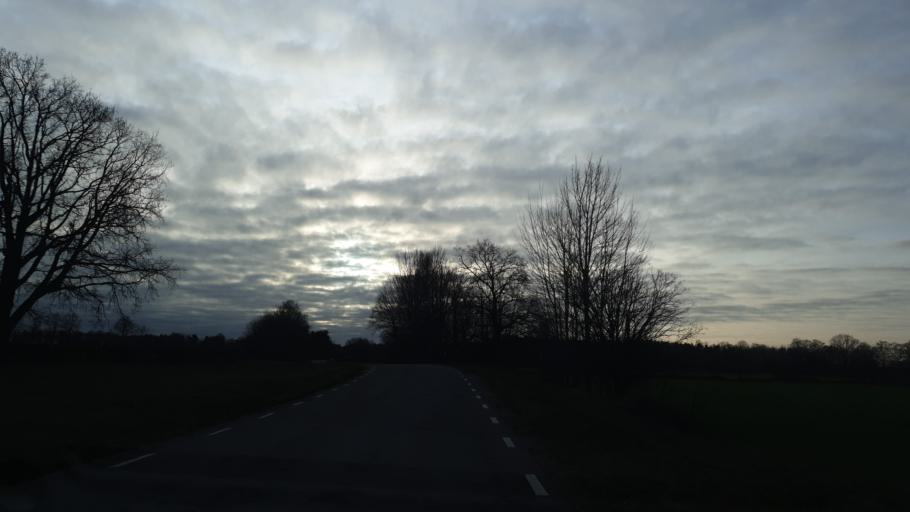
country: SE
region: Kalmar
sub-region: Torsas Kommun
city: Torsas
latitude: 56.3167
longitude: 16.0375
